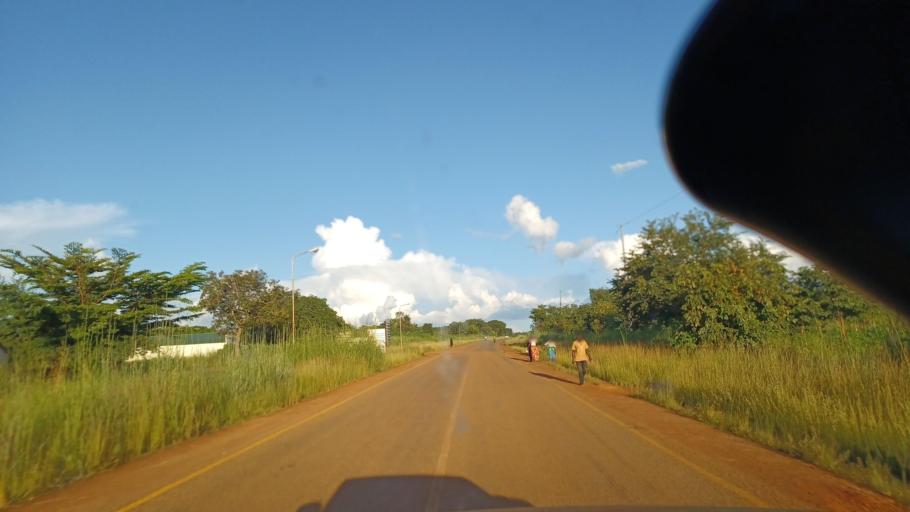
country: ZM
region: North-Western
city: Kalengwa
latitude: -13.1387
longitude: 25.0147
